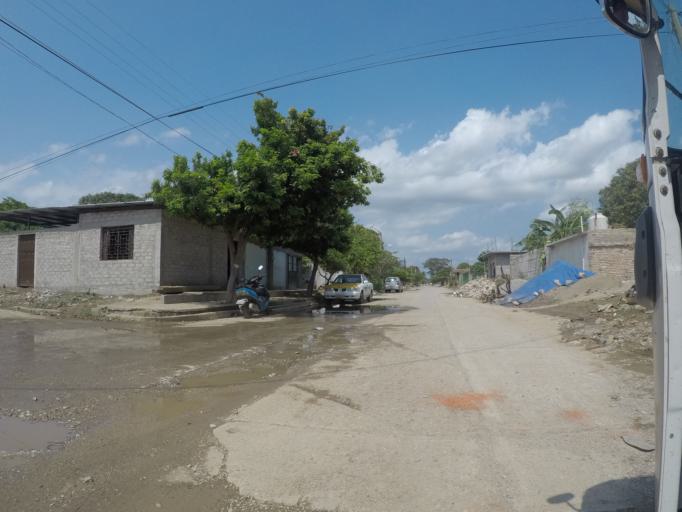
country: MX
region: Oaxaca
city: Union Hidalgo
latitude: 16.4701
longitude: -94.8321
